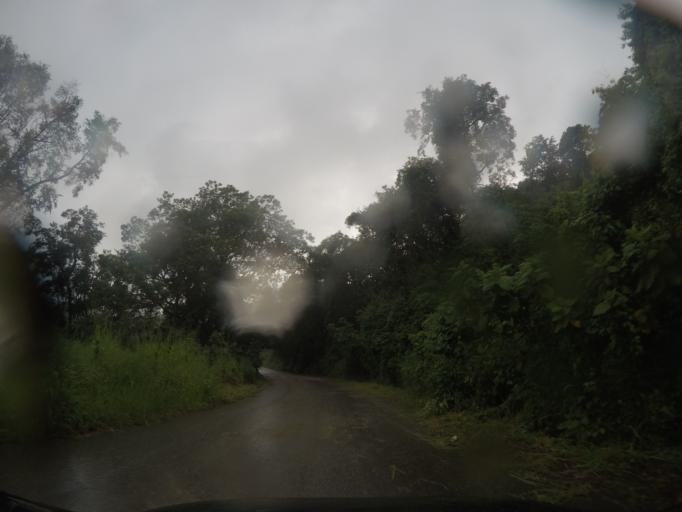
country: MX
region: Oaxaca
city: San Gabriel Mixtepec
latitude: 16.1122
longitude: -97.0667
